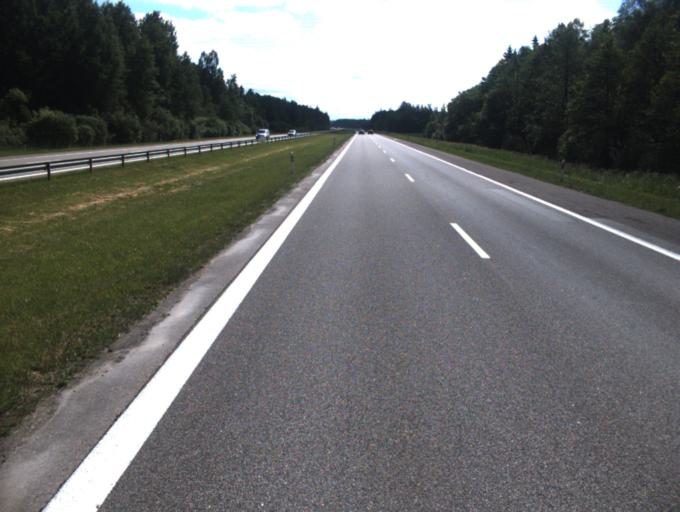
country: LT
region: Klaipedos apskritis
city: Gargzdai
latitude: 55.7018
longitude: 21.6141
